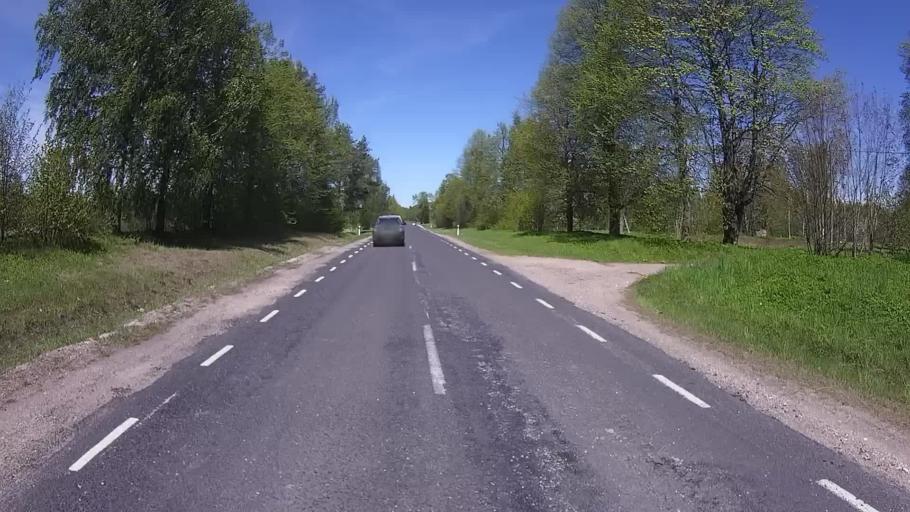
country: EE
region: Polvamaa
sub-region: Raepina vald
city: Rapina
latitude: 58.0425
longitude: 27.3912
